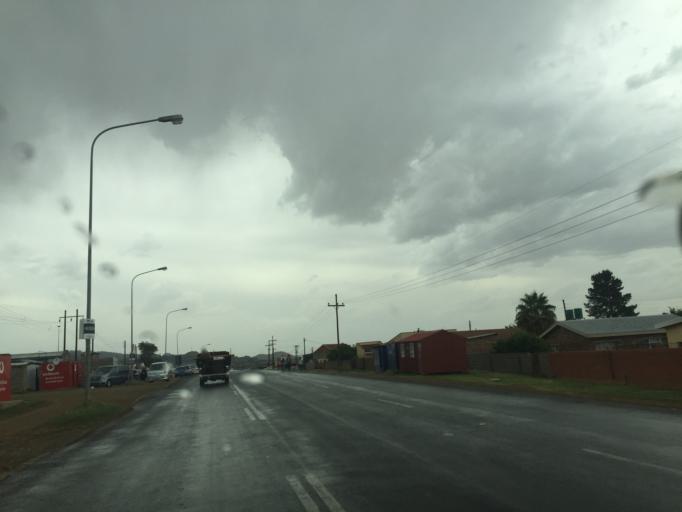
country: LS
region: Maseru
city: Maseru
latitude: -29.2859
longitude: 27.5255
